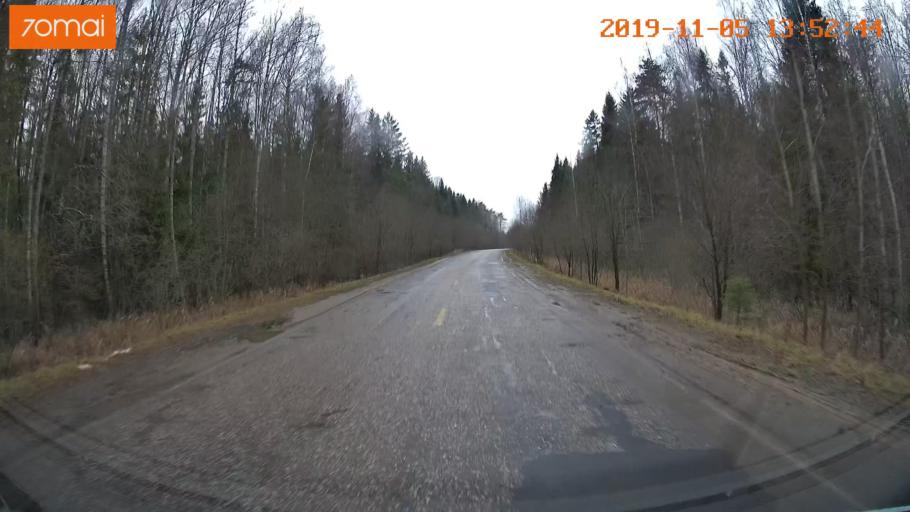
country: RU
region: Ivanovo
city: Kaminskiy
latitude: 57.0287
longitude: 41.3817
